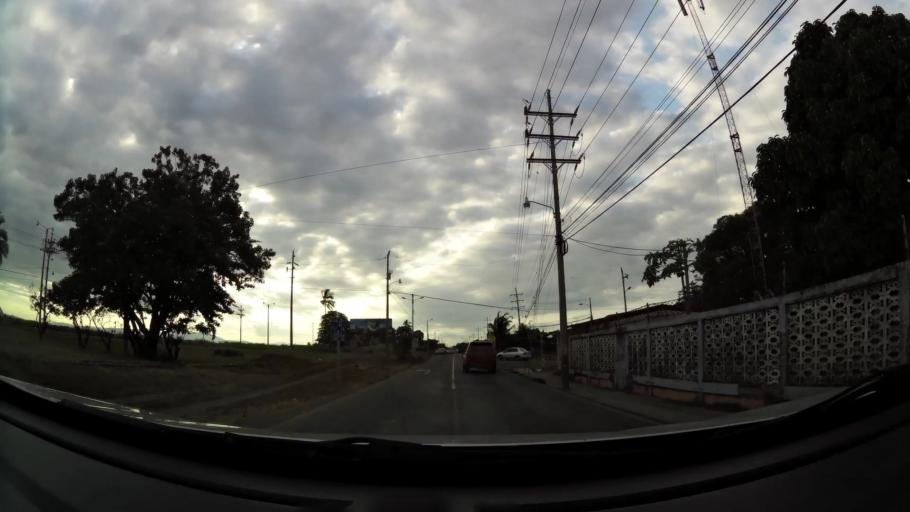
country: CR
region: Puntarenas
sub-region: Canton Central de Puntarenas
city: Chacarita
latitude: 9.9795
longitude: -84.7713
